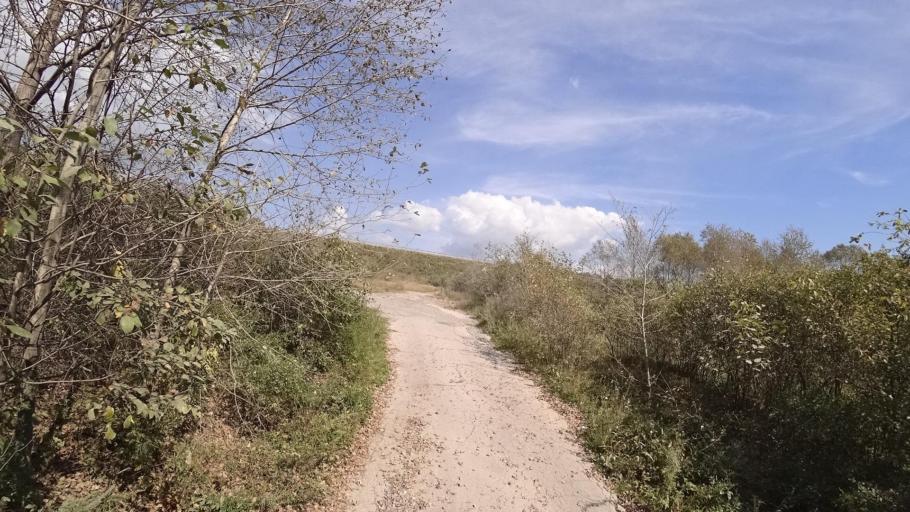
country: RU
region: Jewish Autonomous Oblast
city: Londoko
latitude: 49.0072
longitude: 131.9145
